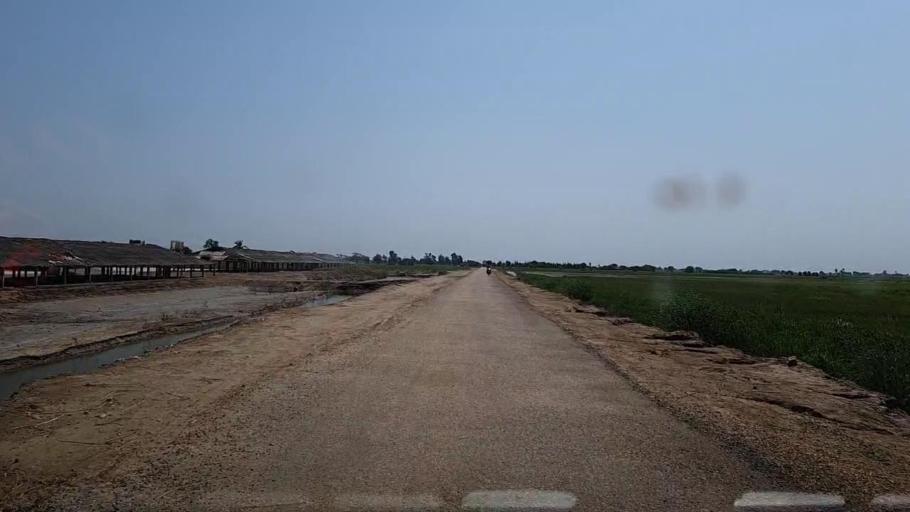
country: PK
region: Sindh
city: Mirpur Batoro
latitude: 24.6213
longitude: 68.4522
